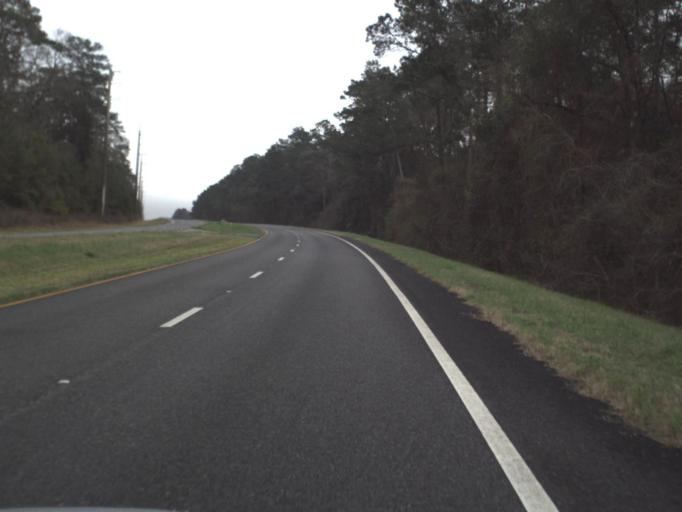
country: US
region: Florida
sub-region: Leon County
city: Woodville
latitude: 30.4022
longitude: -84.0509
